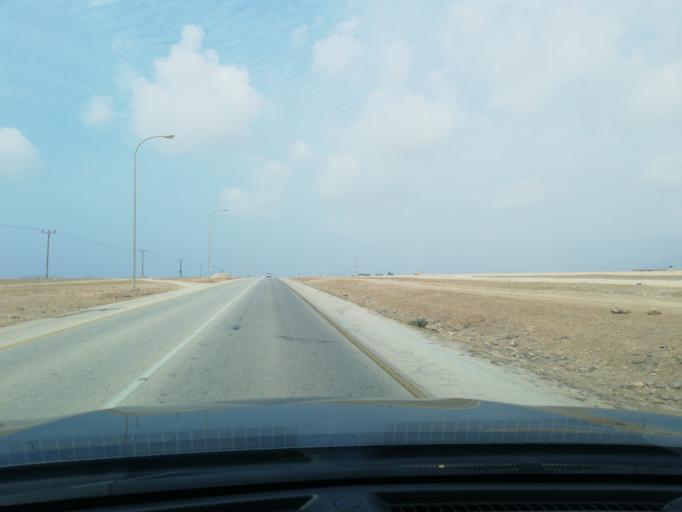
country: OM
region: Zufar
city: Salalah
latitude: 16.9444
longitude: 53.8493
